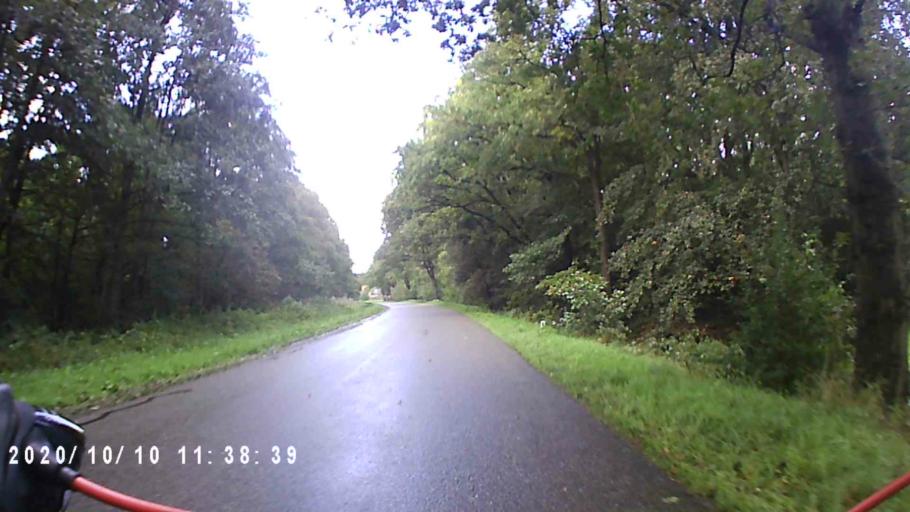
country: NL
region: Friesland
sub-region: Gemeente Smallingerland
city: Drachten
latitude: 53.0709
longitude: 6.1093
